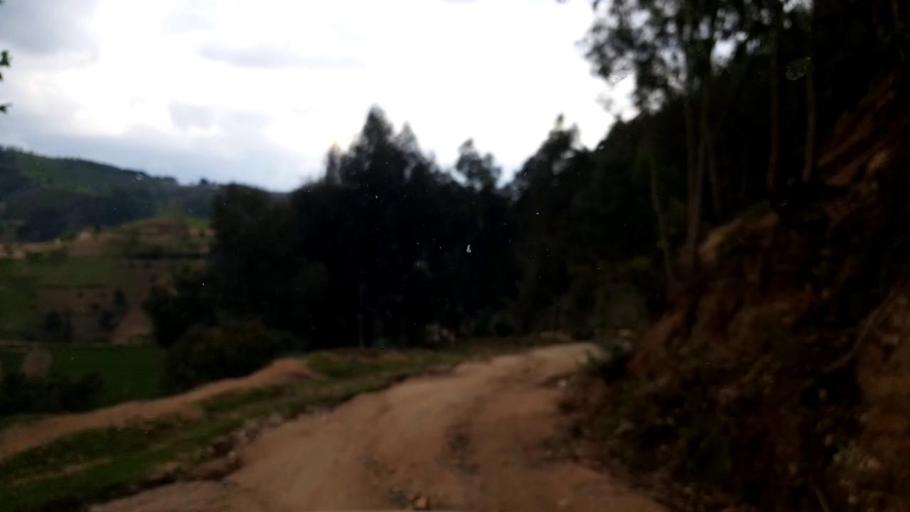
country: RW
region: Western Province
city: Kibuye
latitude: -1.8637
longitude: 29.5548
